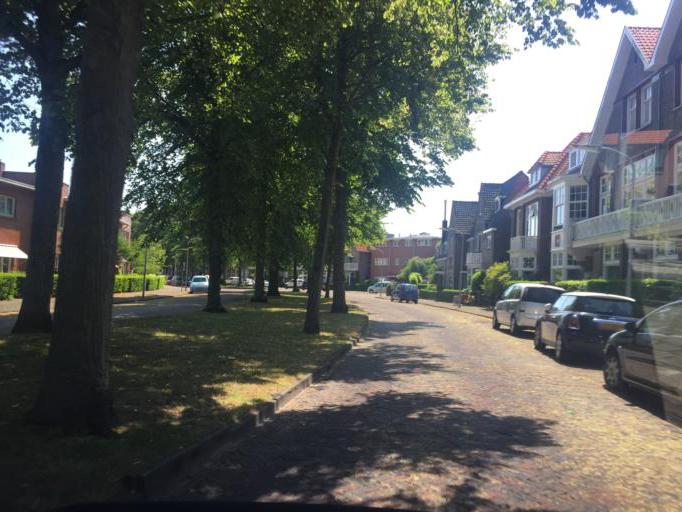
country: NL
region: North Holland
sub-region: Gemeente Bloemendaal
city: Bloemendaal
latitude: 52.3936
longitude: 4.6257
